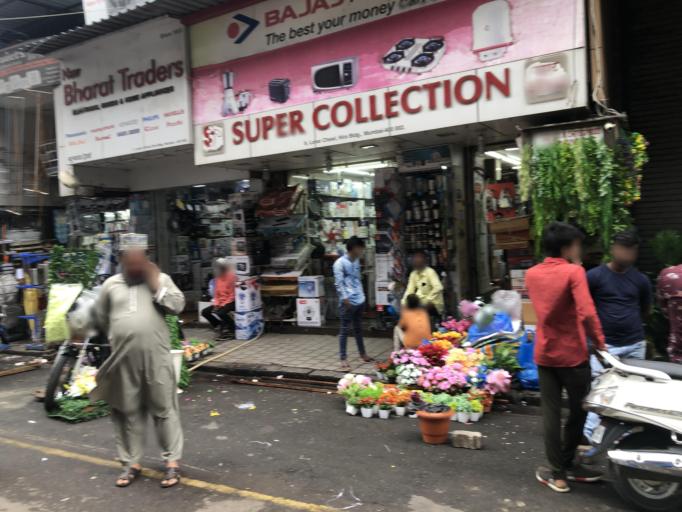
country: IN
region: Maharashtra
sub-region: Raigarh
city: Uran
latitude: 18.9471
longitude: 72.8330
